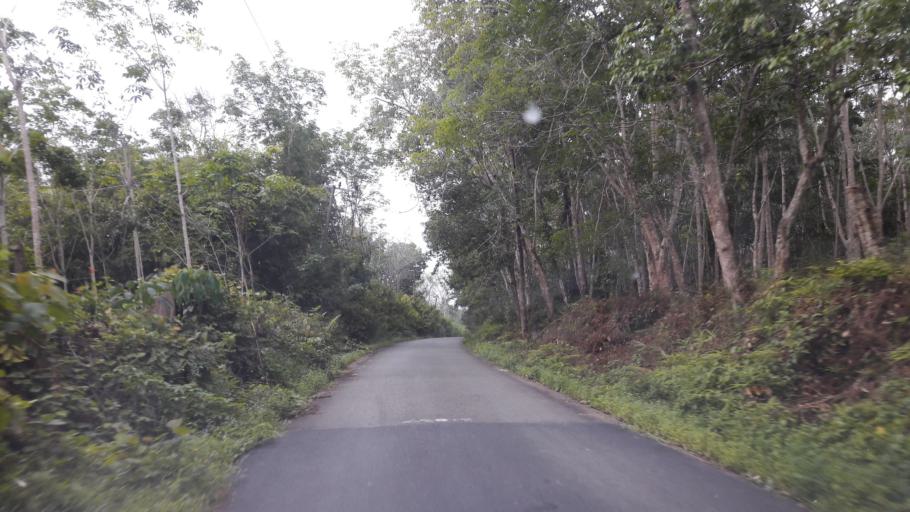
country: ID
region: South Sumatra
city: Gunungmenang
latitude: -3.1262
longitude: 104.1120
